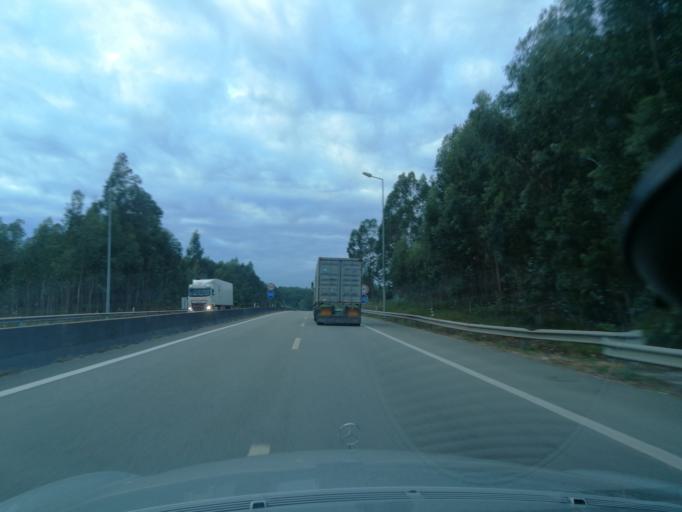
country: PT
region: Aveiro
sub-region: Albergaria-A-Velha
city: Albergaria-a-Velha
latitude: 40.6762
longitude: -8.4775
